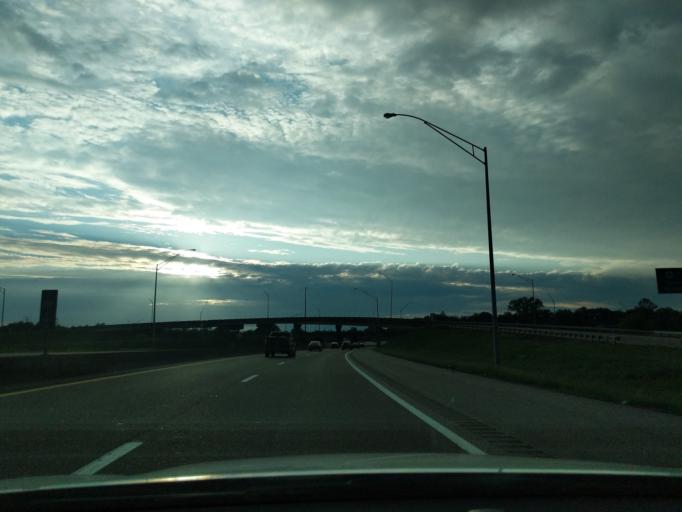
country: US
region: Tennessee
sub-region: Shelby County
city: New South Memphis
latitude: 35.0784
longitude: -90.0547
